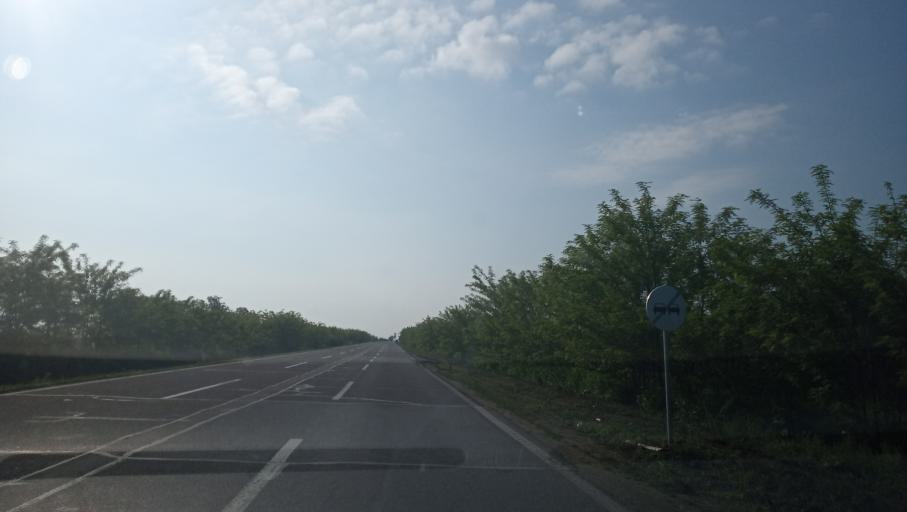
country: RO
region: Timis
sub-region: Comuna Moravita
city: Moravita
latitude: 45.2269
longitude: 21.2852
